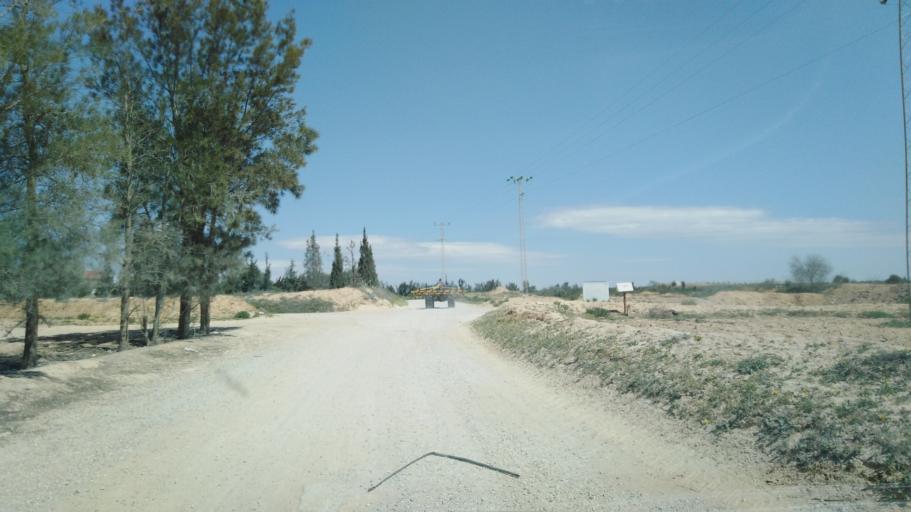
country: TN
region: Safaqis
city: Sfax
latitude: 34.7584
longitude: 10.5289
